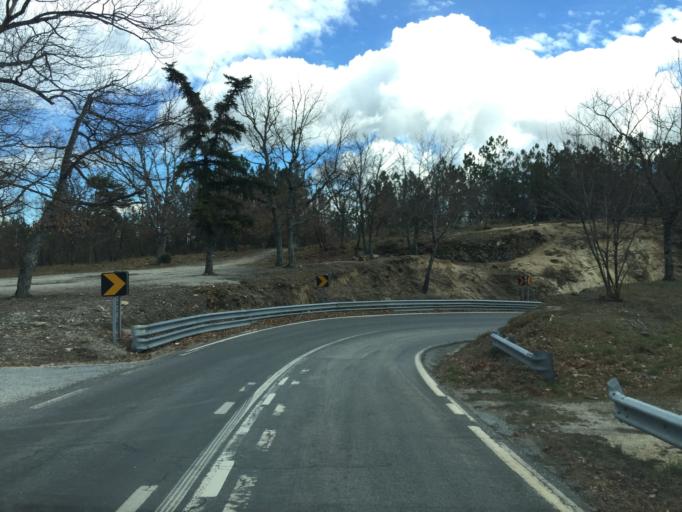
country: PT
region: Castelo Branco
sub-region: Covilha
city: Covilha
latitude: 40.2861
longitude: -7.5237
